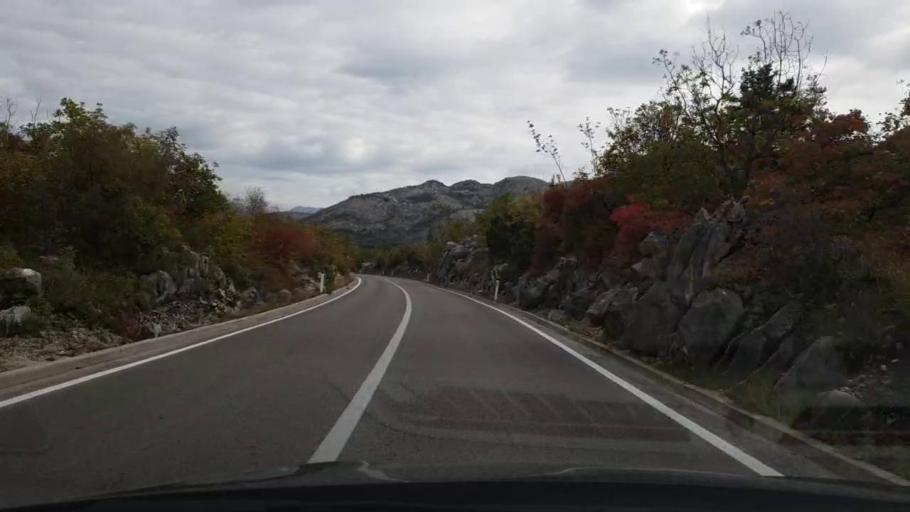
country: BA
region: Republika Srpska
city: Trebinje
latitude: 42.6891
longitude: 18.2771
